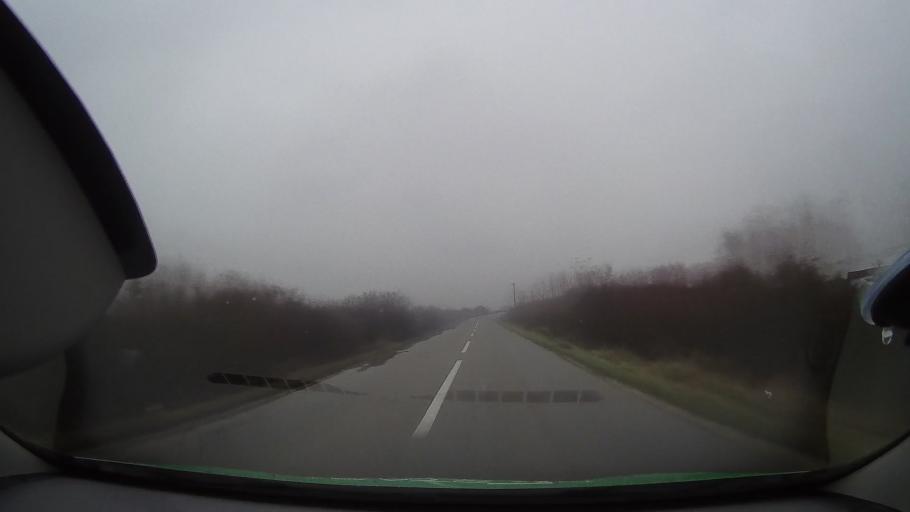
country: RO
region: Bihor
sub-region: Comuna Madaras
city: Madaras
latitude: 46.7954
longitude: 21.7215
